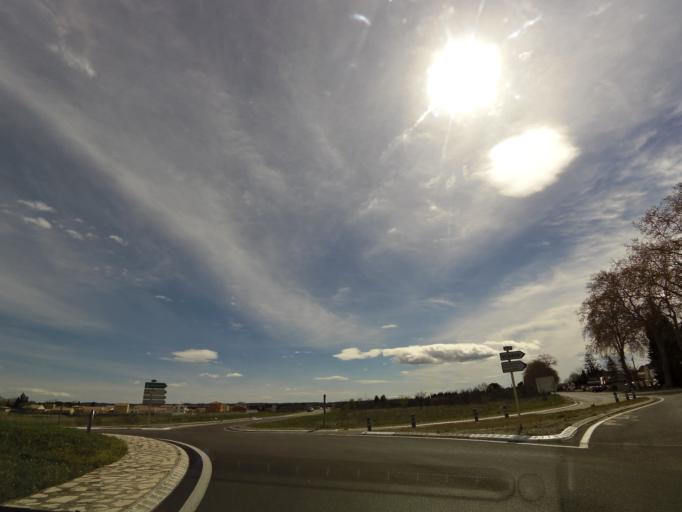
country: FR
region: Languedoc-Roussillon
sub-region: Departement du Gard
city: Bernis
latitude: 43.7678
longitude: 4.2781
